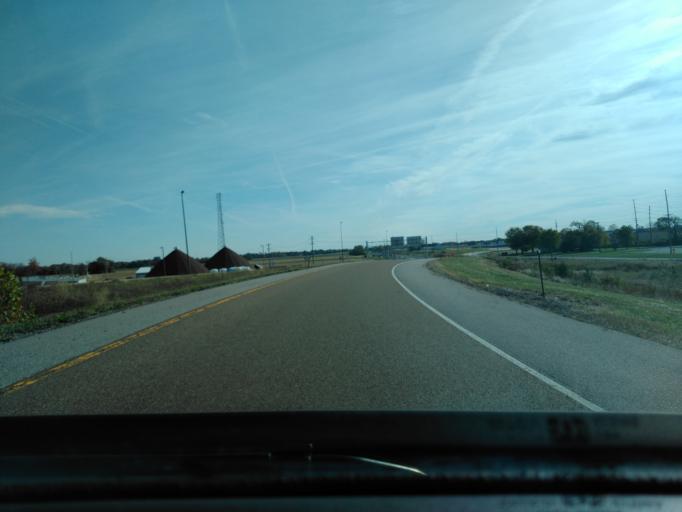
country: US
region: Illinois
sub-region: Madison County
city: Troy
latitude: 38.7178
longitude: -89.9169
